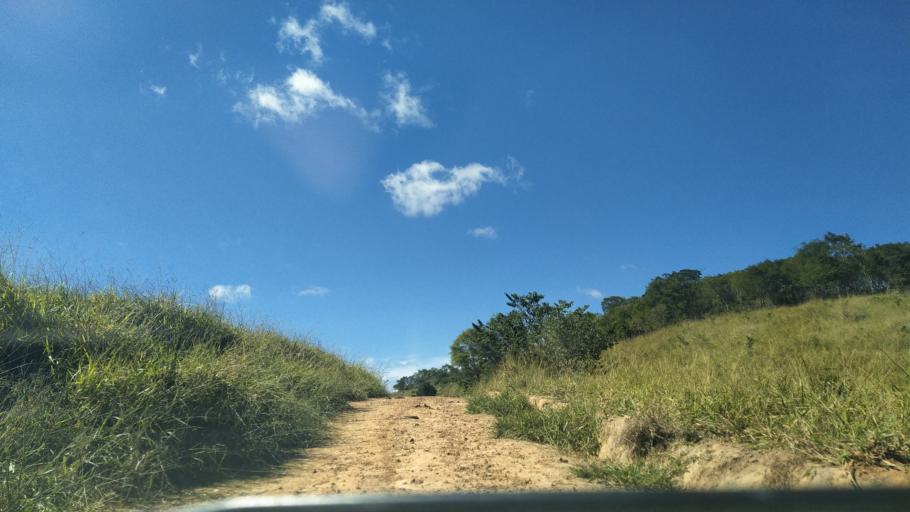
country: BR
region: Minas Gerais
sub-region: Almenara
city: Almenara
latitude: -16.6130
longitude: -40.4591
